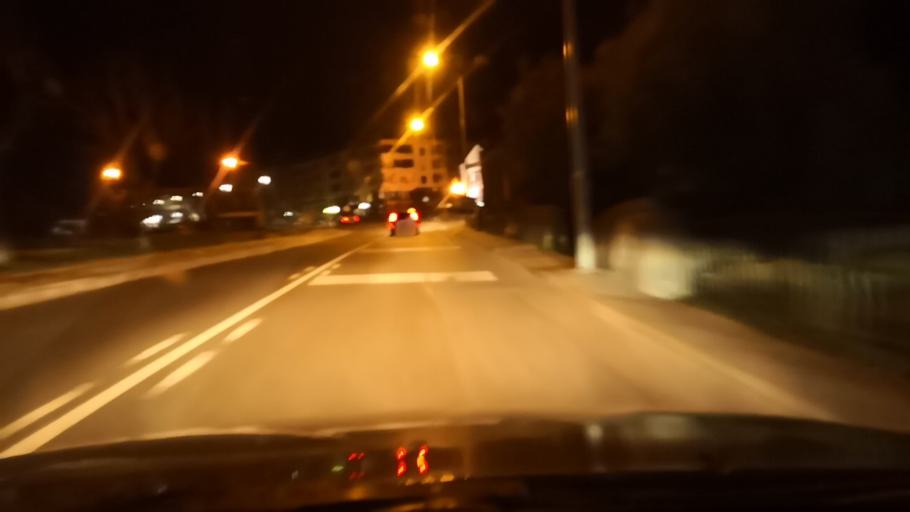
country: PT
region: Castelo Branco
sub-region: Concelho do Fundao
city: Fundao
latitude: 40.1512
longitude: -7.4978
